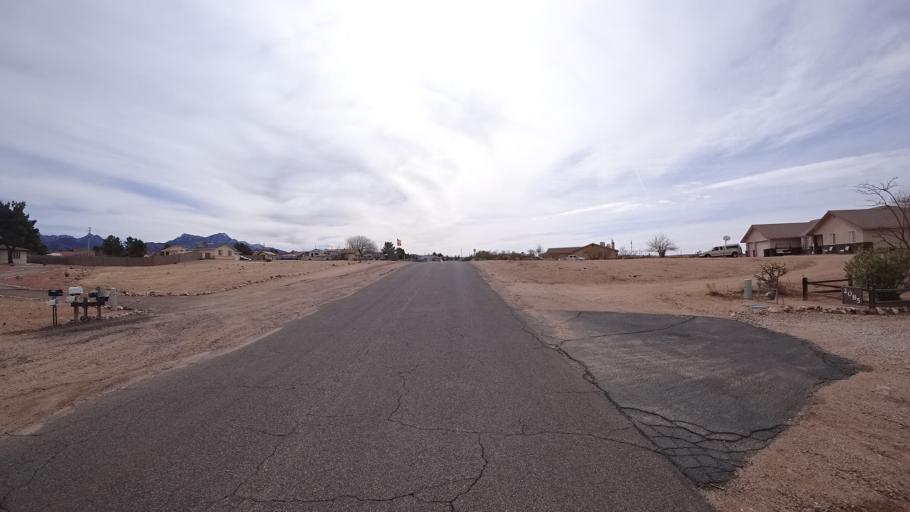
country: US
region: Arizona
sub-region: Mohave County
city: Kingman
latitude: 35.1853
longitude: -113.9927
